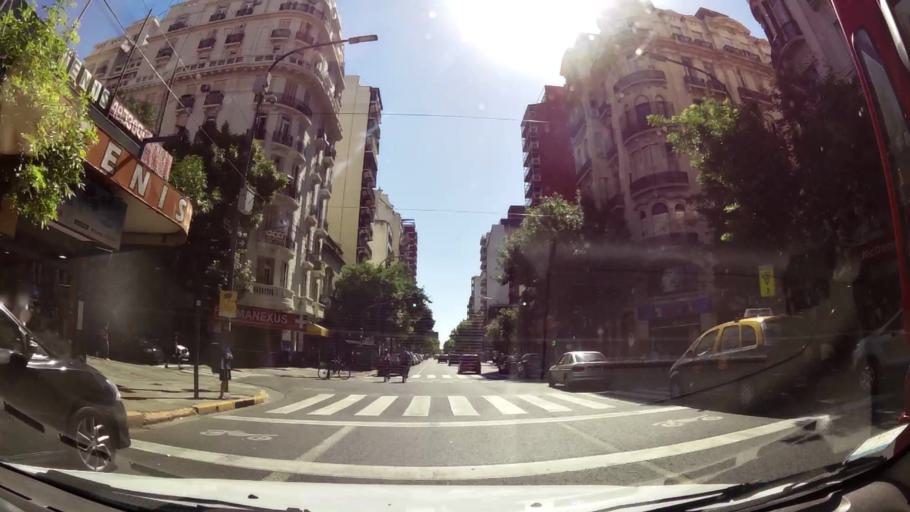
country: AR
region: Buenos Aires F.D.
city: Buenos Aires
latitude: -34.6096
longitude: -58.3974
